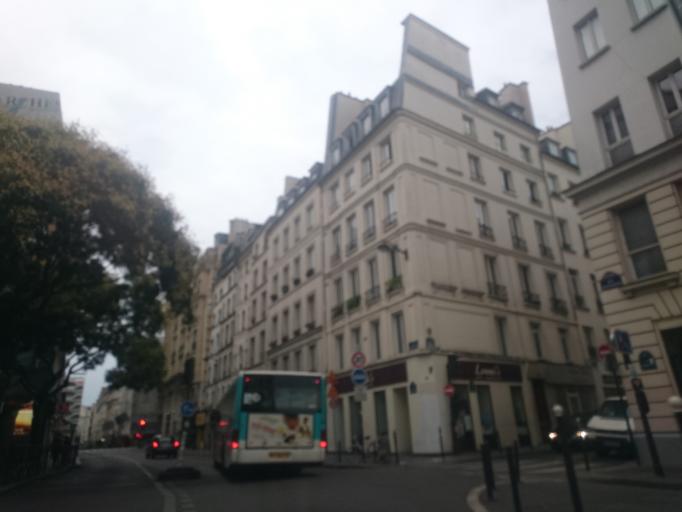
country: FR
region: Ile-de-France
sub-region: Paris
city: Paris
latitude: 48.8673
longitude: 2.3438
